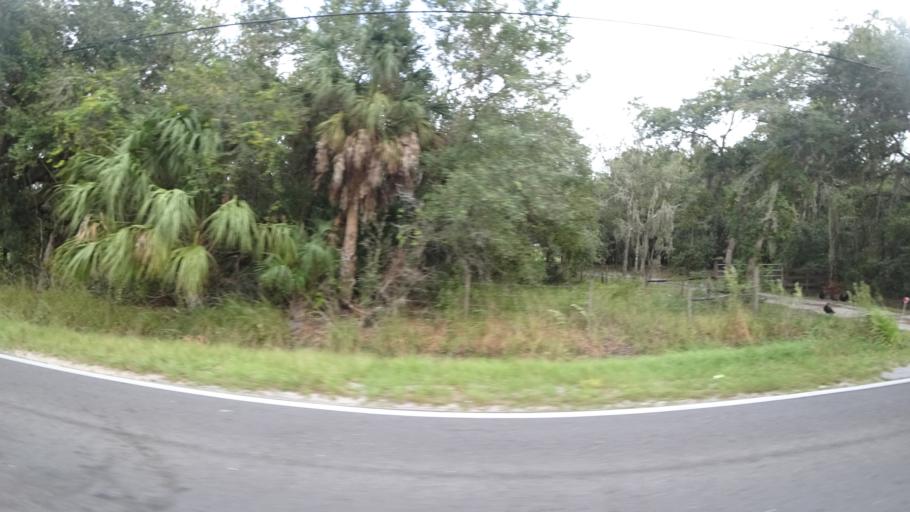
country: US
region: Florida
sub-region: Manatee County
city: Ellenton
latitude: 27.5623
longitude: -82.4789
